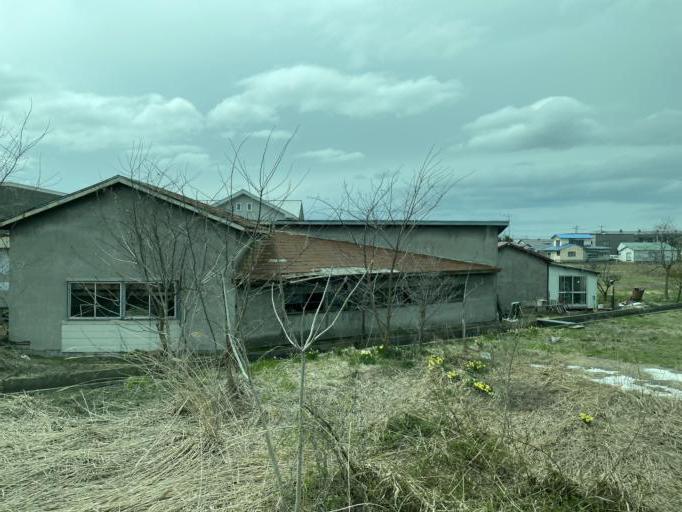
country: JP
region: Aomori
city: Goshogawara
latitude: 40.7603
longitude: 140.4357
